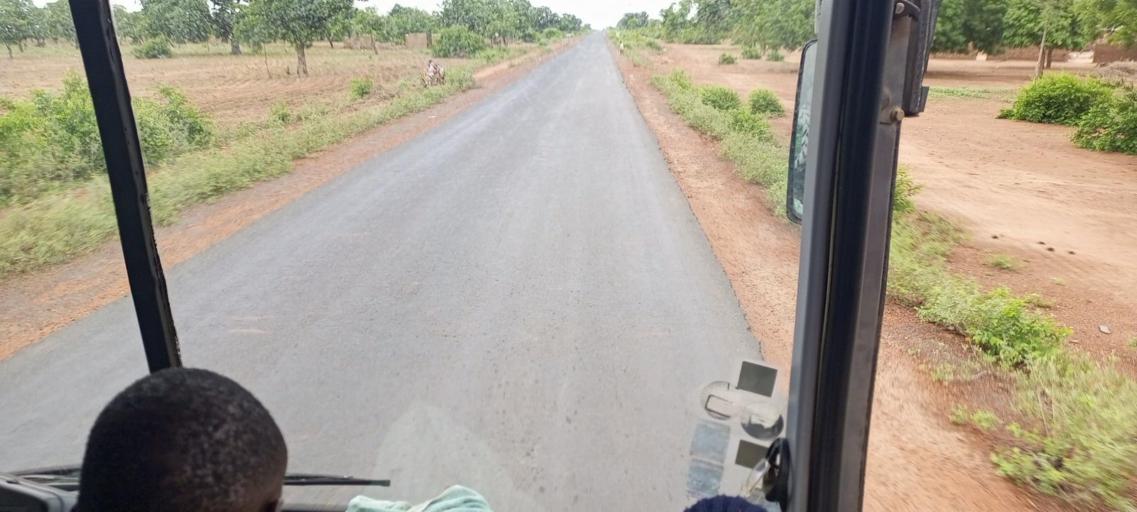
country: ML
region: Sikasso
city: Koutiala
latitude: 12.5761
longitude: -5.6068
